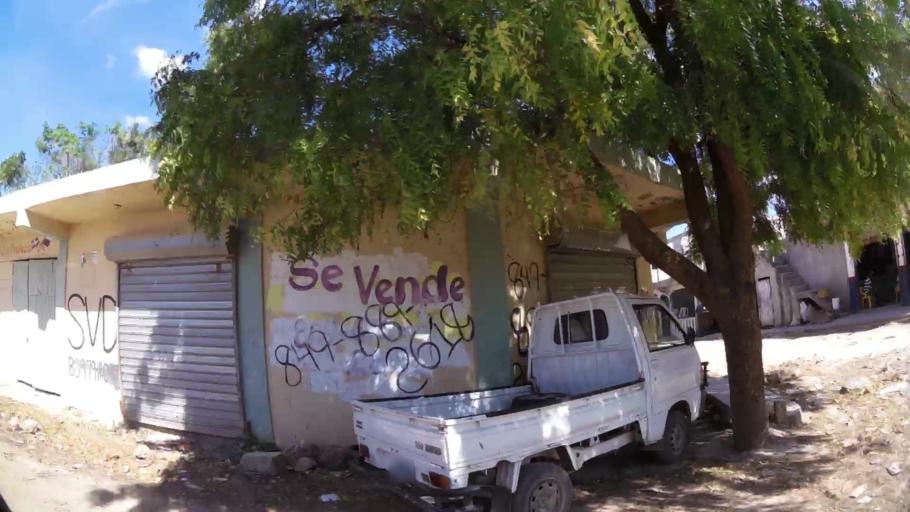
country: DO
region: Santo Domingo
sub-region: Santo Domingo
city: Santo Domingo Este
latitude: 18.4715
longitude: -69.7669
